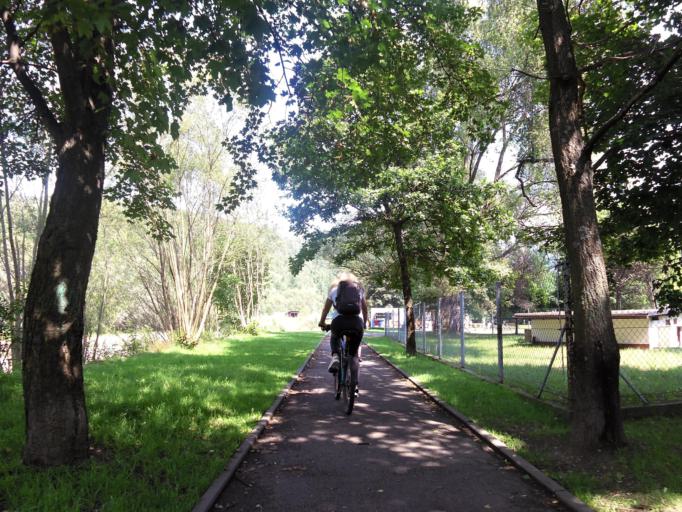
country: PL
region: Silesian Voivodeship
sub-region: Powiat zywiecki
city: Rajcza
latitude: 49.5050
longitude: 19.0997
